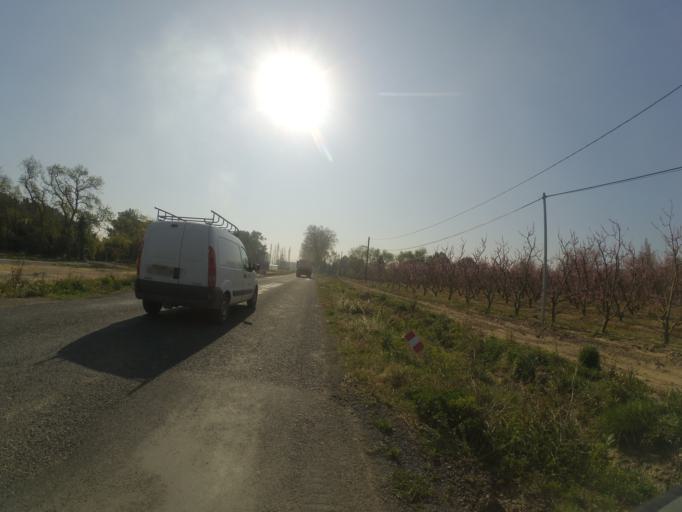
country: FR
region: Languedoc-Roussillon
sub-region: Departement des Pyrenees-Orientales
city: Thuir
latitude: 42.6444
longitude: 2.7397
